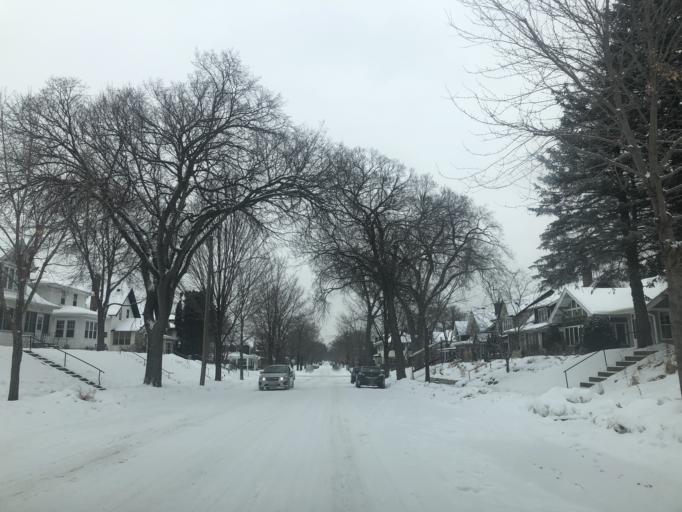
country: US
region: Minnesota
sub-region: Hennepin County
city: Richfield
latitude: 44.9295
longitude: -93.2831
